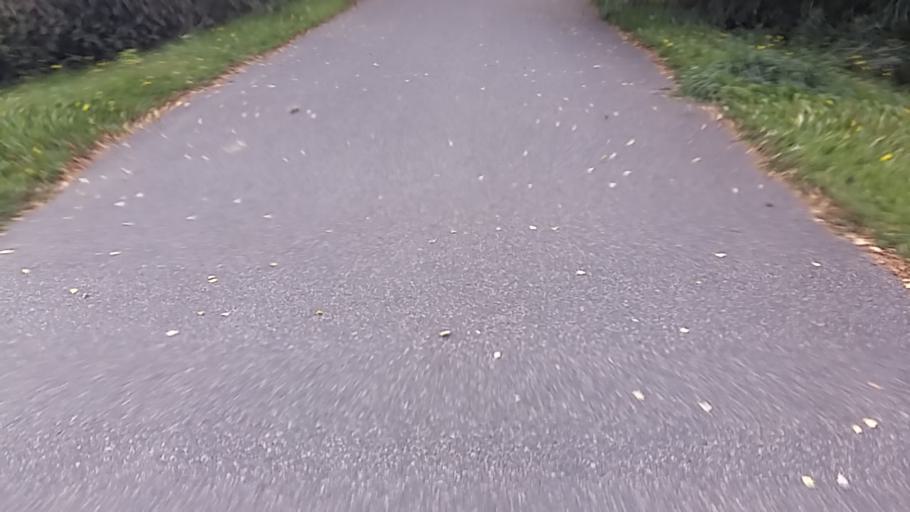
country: SE
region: Joenkoeping
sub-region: Jonkopings Kommun
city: Odensjo
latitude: 57.7376
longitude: 14.1537
